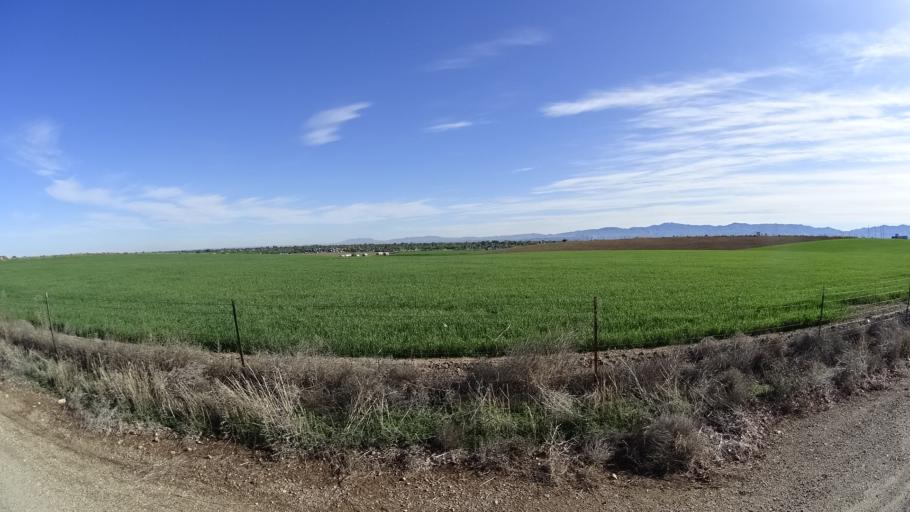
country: US
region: Idaho
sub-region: Ada County
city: Garden City
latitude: 43.5248
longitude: -116.2872
